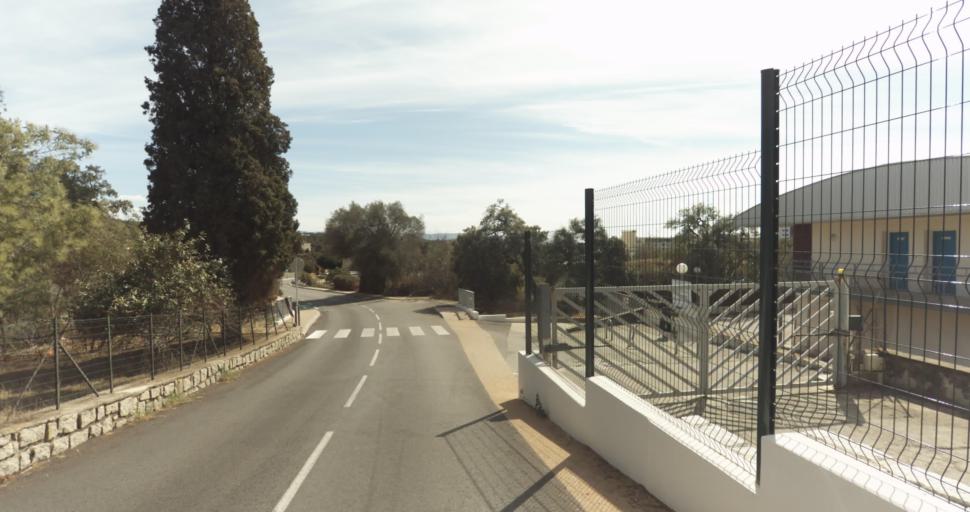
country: FR
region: Corsica
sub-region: Departement de la Corse-du-Sud
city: Ajaccio
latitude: 41.9481
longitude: 8.7574
